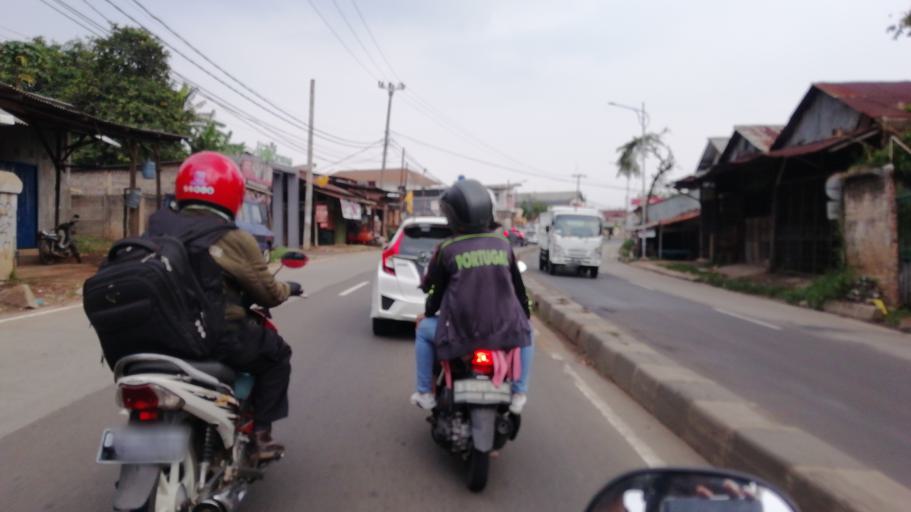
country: ID
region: West Java
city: Parung
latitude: -6.4942
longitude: 106.7499
